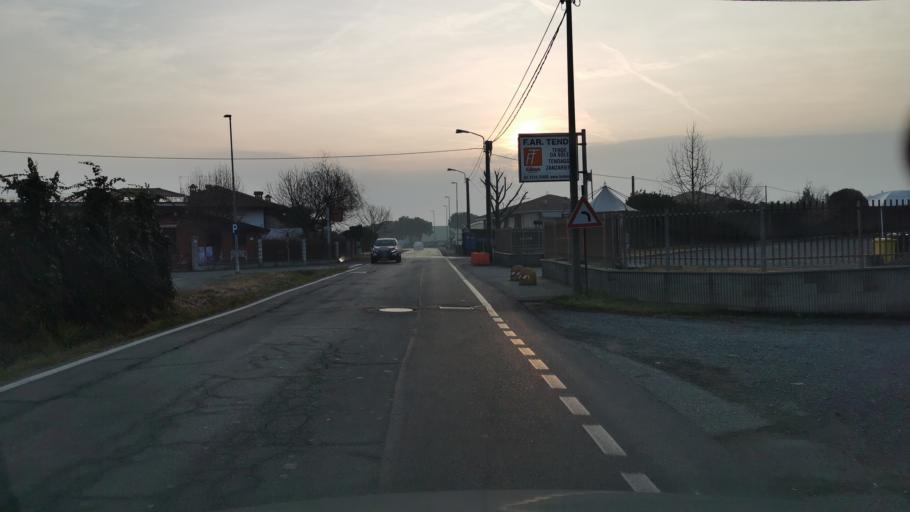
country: IT
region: Piedmont
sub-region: Provincia di Torino
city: Ozegna
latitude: 45.3467
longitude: 7.7473
